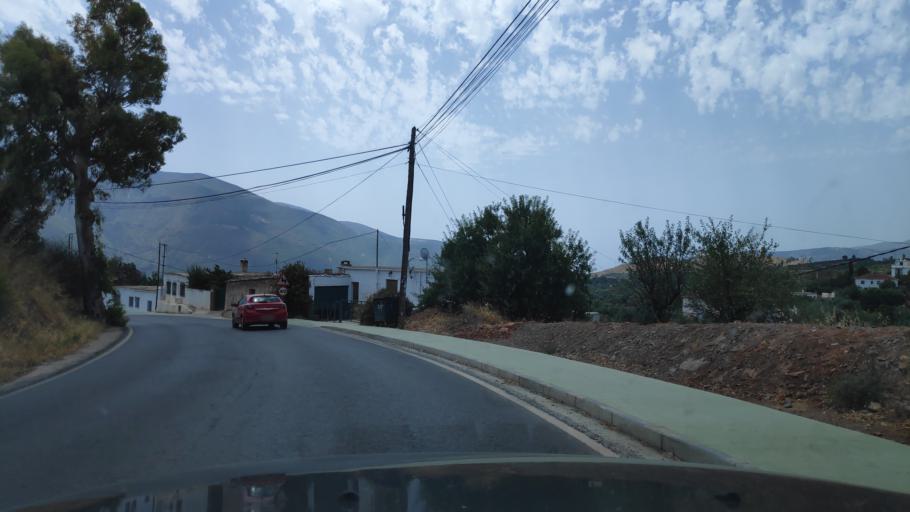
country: ES
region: Andalusia
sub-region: Provincia de Granada
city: Orjiva
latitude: 36.9032
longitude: -3.4328
